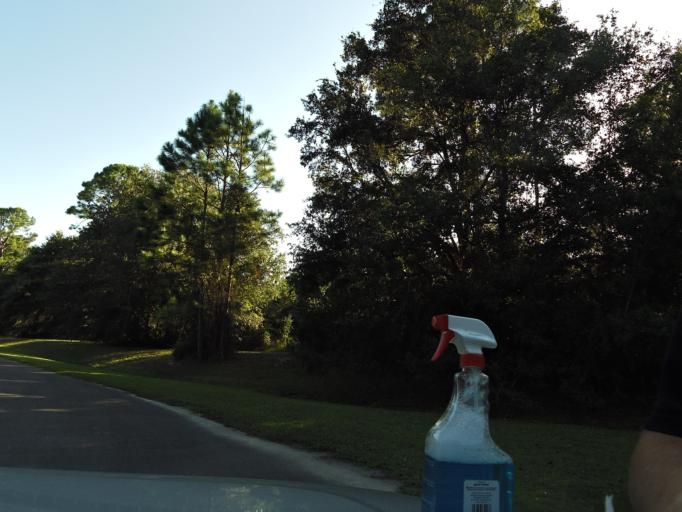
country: US
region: Florida
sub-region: Franklin County
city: Eastpoint
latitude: 29.7604
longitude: -84.8305
